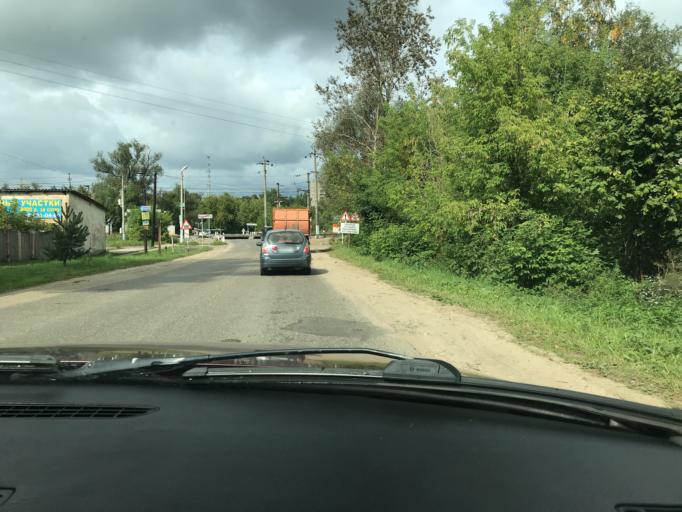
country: RU
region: Kaluga
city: Maloyaroslavets
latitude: 54.9961
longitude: 36.4711
